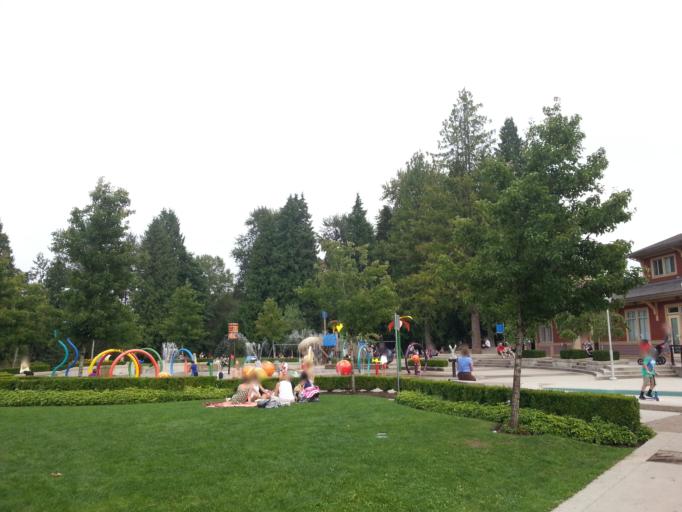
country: CA
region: British Columbia
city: Port Moody
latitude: 49.2797
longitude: -122.8486
